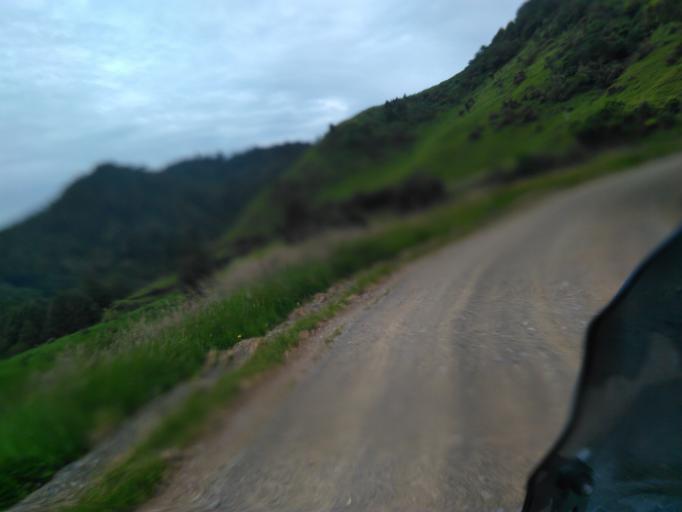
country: NZ
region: Bay of Plenty
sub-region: Opotiki District
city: Opotiki
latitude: -38.1026
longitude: 177.4895
